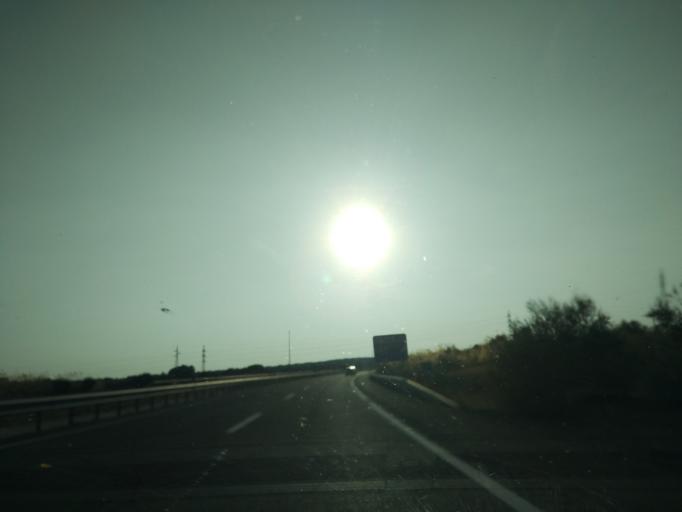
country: ES
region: Castille and Leon
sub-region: Provincia de Avila
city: Berrocalejo de Aragona
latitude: 40.6746
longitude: -4.6159
